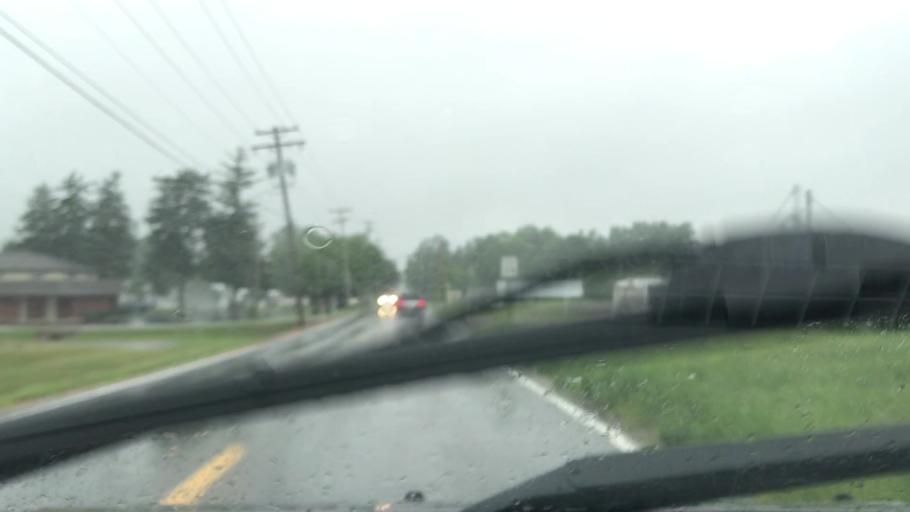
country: US
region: Indiana
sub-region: Hamilton County
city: Sheridan
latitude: 40.1299
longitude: -86.2158
